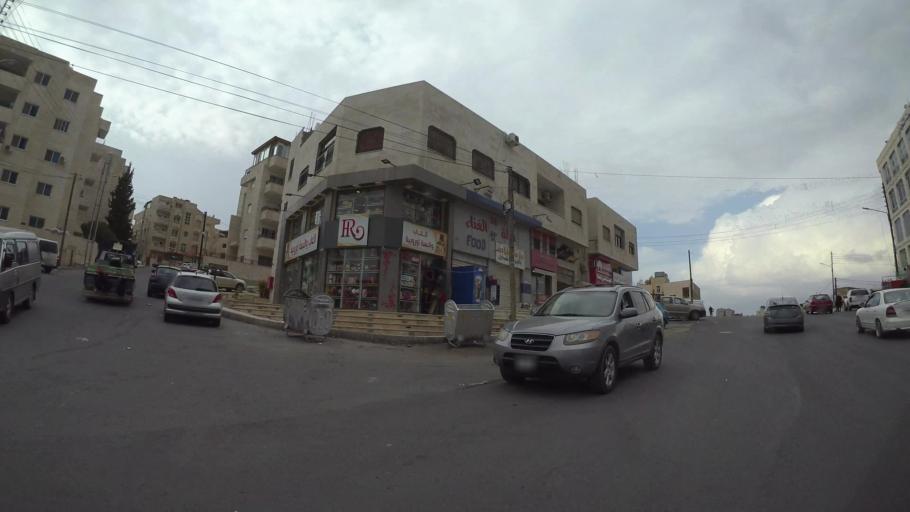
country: JO
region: Amman
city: Amman
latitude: 32.0035
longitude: 35.9498
